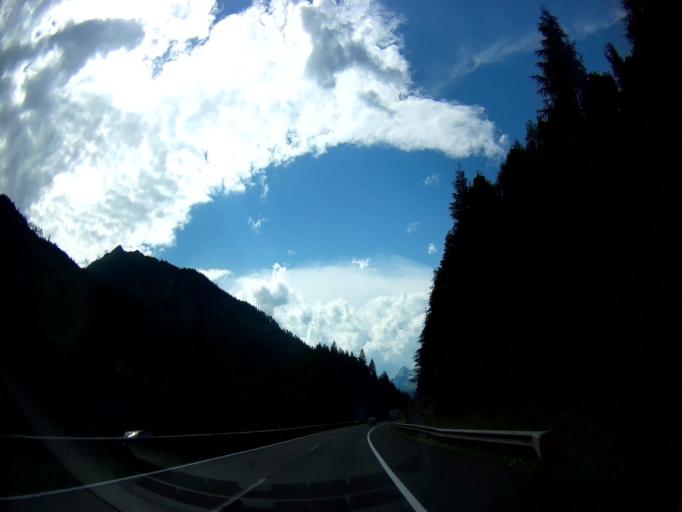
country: AT
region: Salzburg
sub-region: Politischer Bezirk Tamsweg
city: Zederhaus
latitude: 47.1421
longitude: 13.5261
